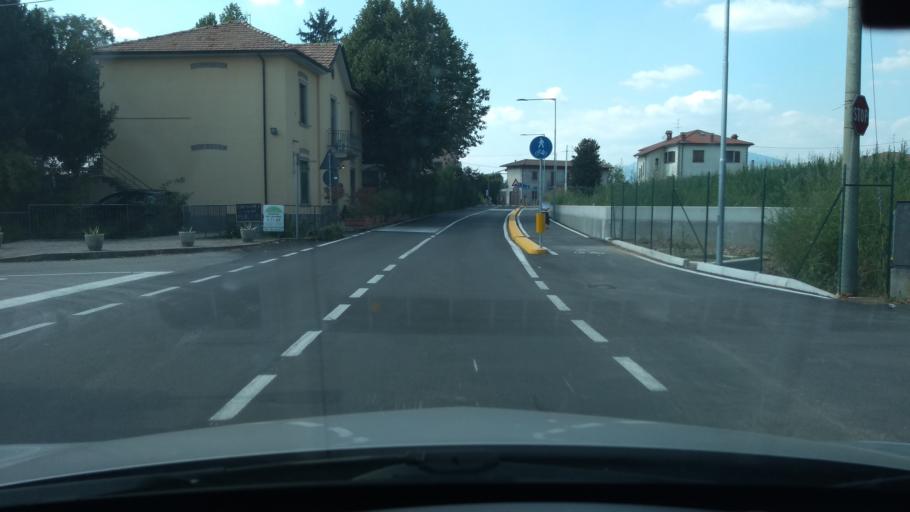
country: IT
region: Lombardy
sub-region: Provincia di Bergamo
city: Lallio
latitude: 45.6608
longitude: 9.6402
